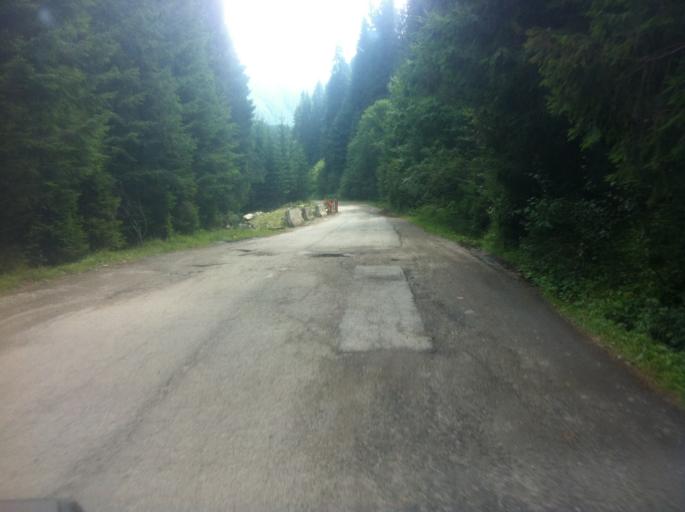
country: RO
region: Hunedoara
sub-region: Oras Petrila
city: Petrila
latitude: 45.4100
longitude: 23.5530
